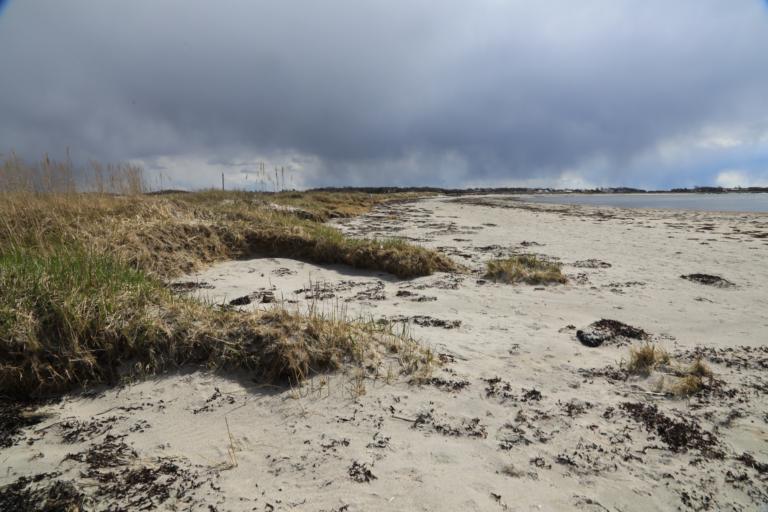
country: SE
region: Halland
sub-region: Varbergs Kommun
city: Varberg
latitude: 57.0831
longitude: 12.2579
